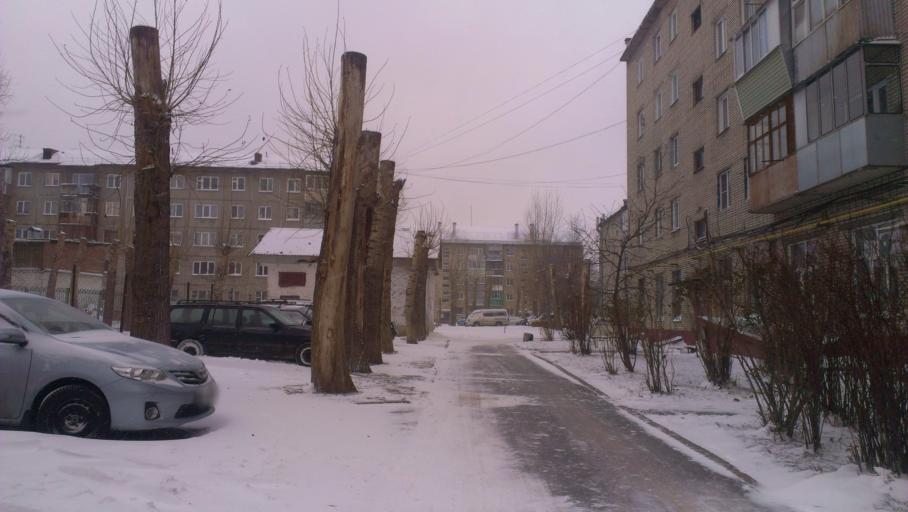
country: RU
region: Altai Krai
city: Novosilikatnyy
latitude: 53.3658
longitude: 83.6793
